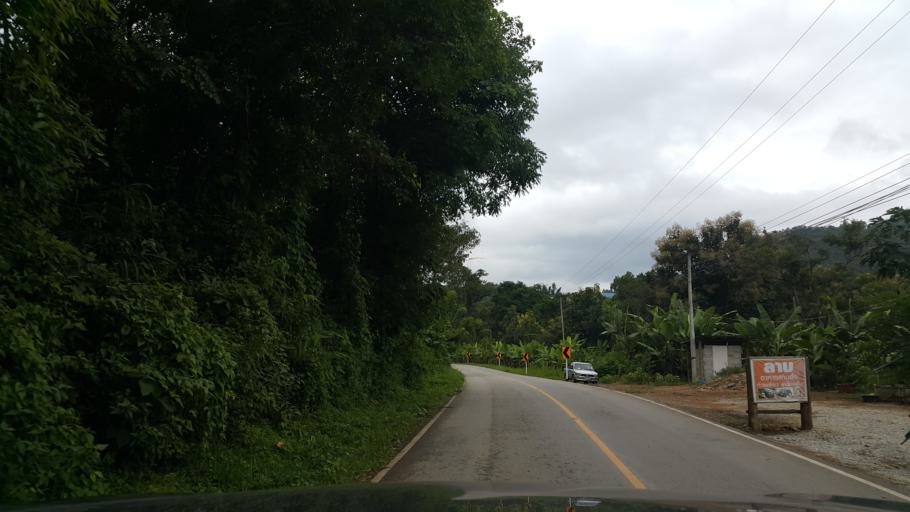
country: TH
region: Chiang Mai
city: Samoeng
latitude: 18.8641
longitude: 98.6398
